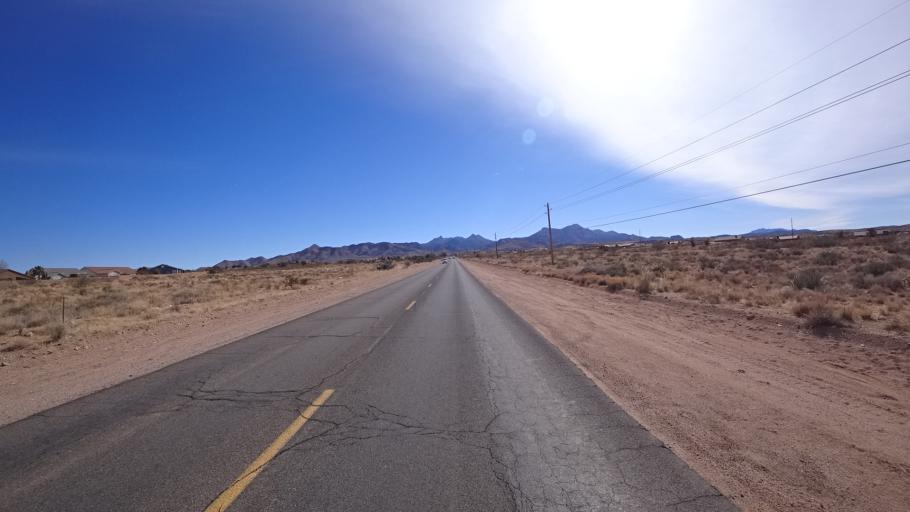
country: US
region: Arizona
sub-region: Mohave County
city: Kingman
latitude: 35.1839
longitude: -114.0021
